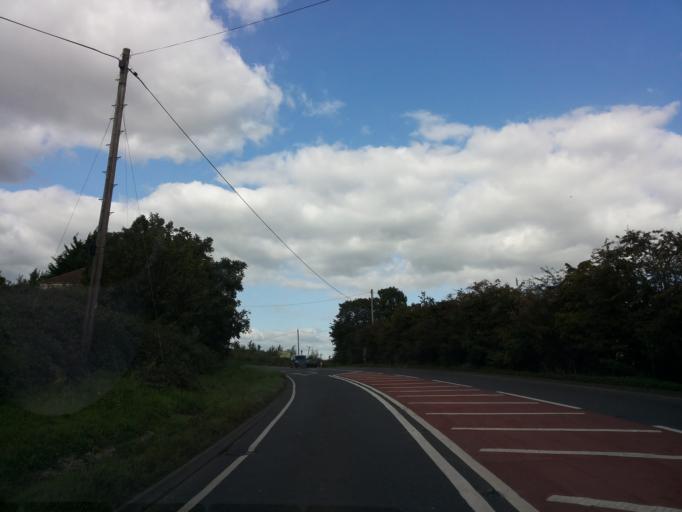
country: GB
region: England
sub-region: Bath and North East Somerset
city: Hinton Charterhouse
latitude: 51.3099
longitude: -2.3059
